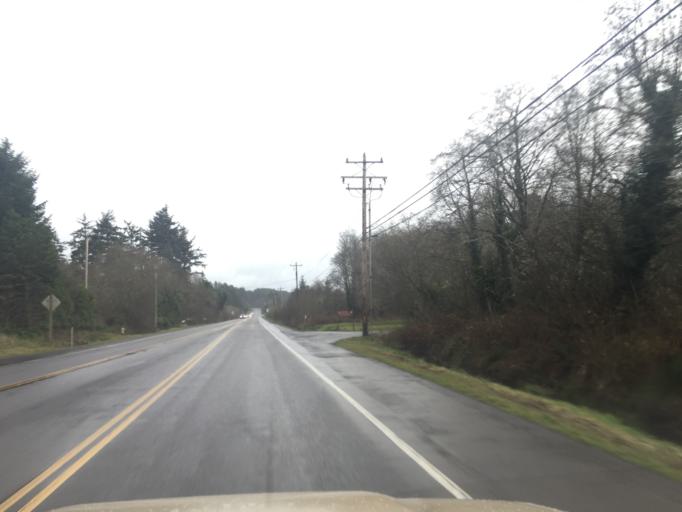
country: US
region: Oregon
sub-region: Lincoln County
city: Newport
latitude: 44.5991
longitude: -124.0589
